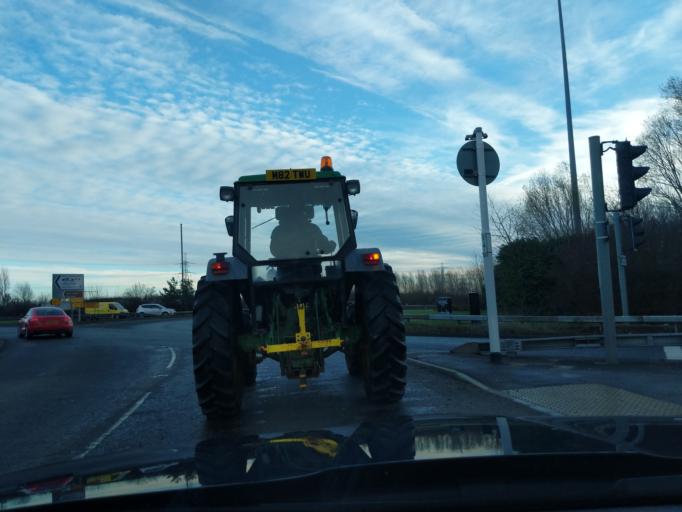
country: GB
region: England
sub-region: South Tyneside
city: Jarrow
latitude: 55.0001
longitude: -1.4858
